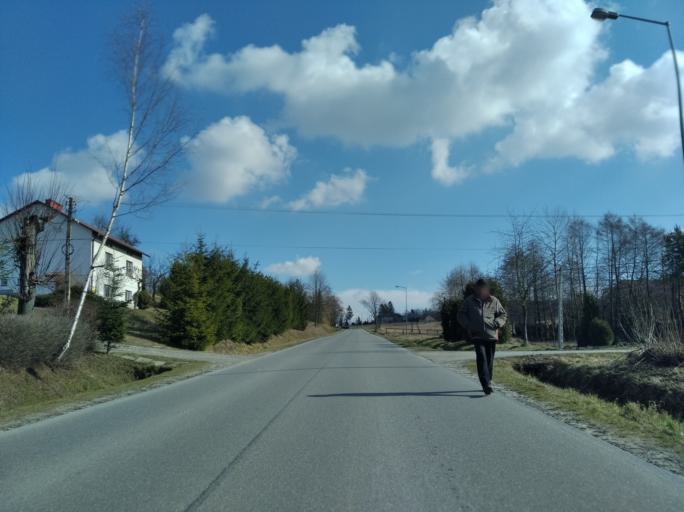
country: PL
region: Subcarpathian Voivodeship
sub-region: Powiat strzyzowski
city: Frysztak
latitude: 49.8497
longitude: 21.5206
